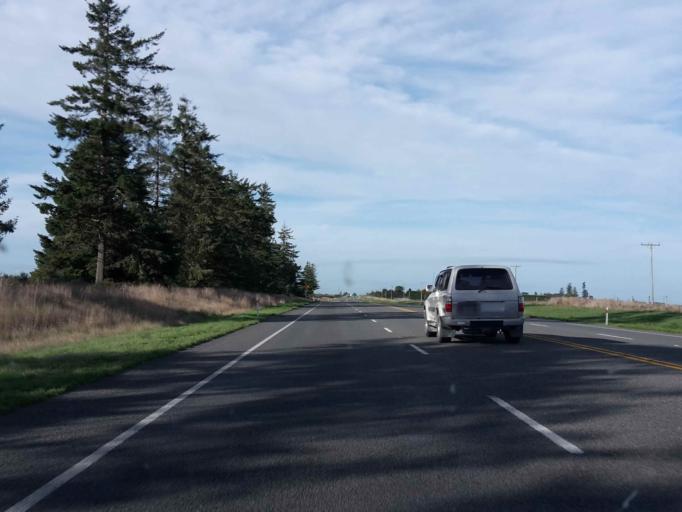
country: NZ
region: Canterbury
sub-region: Ashburton District
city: Tinwald
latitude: -44.0414
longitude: 171.4330
